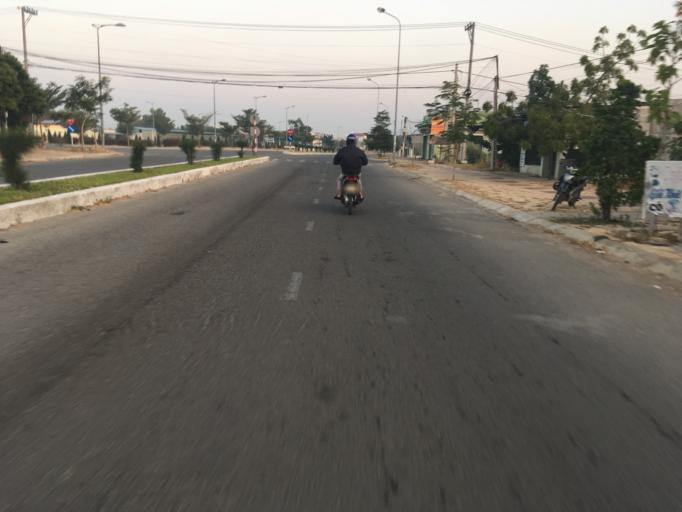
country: VN
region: Ninh Thuan
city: Phan Rang-Thap Cham
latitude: 11.5576
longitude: 109.0221
